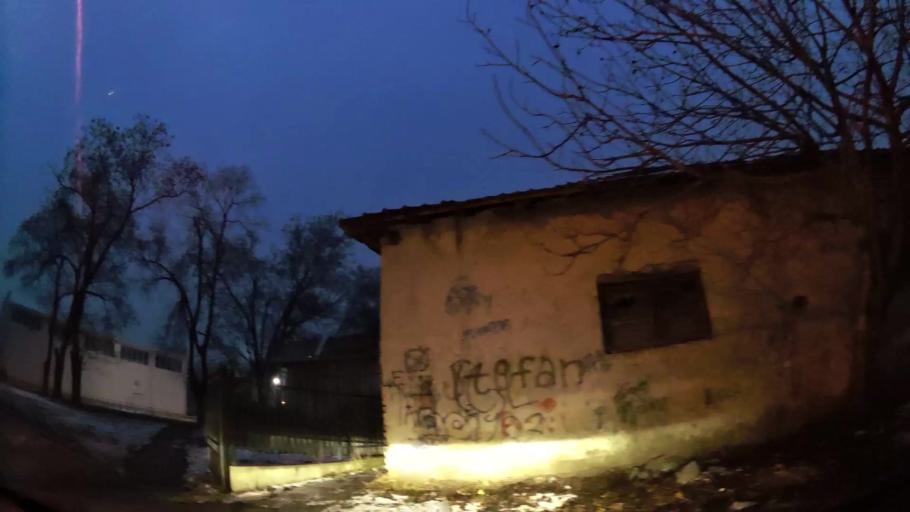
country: MK
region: Kisela Voda
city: Kisela Voda
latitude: 41.9705
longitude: 21.4865
